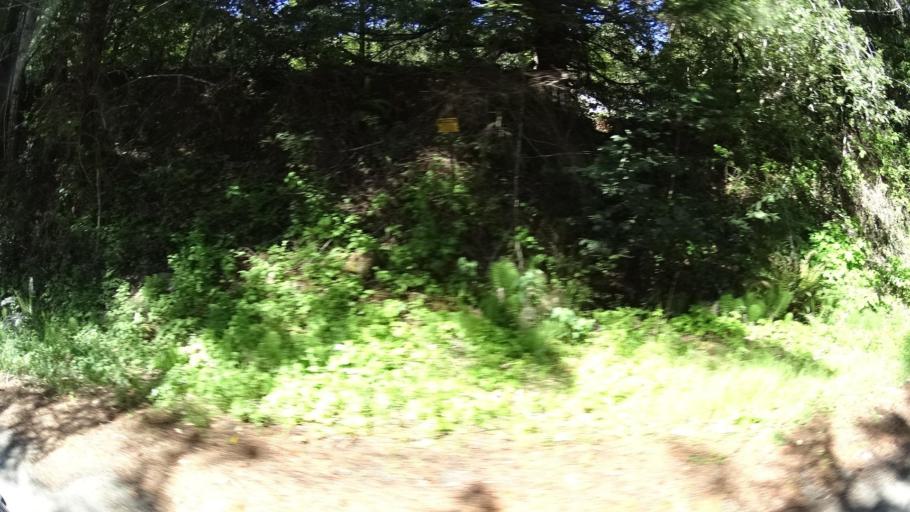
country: US
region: California
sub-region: Humboldt County
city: Rio Dell
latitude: 40.2318
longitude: -124.1536
